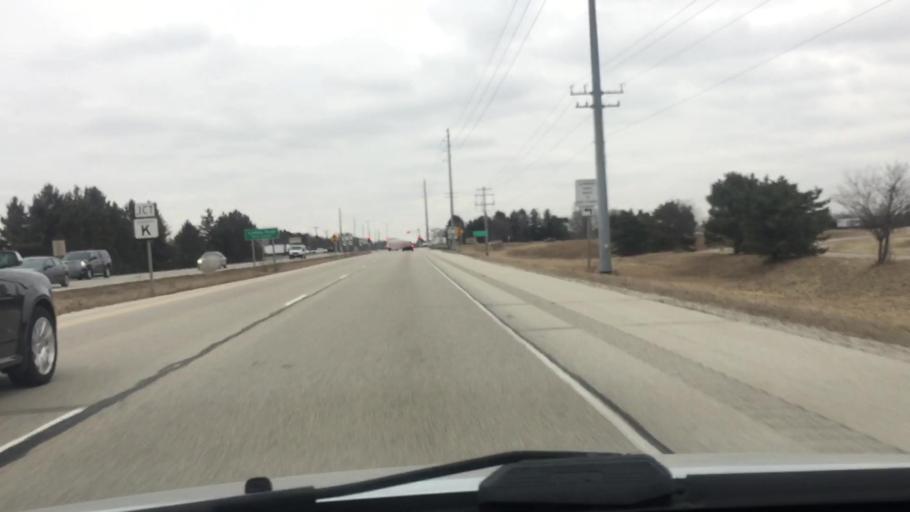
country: US
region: Wisconsin
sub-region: Waukesha County
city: Sussex
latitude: 43.1092
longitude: -88.2102
